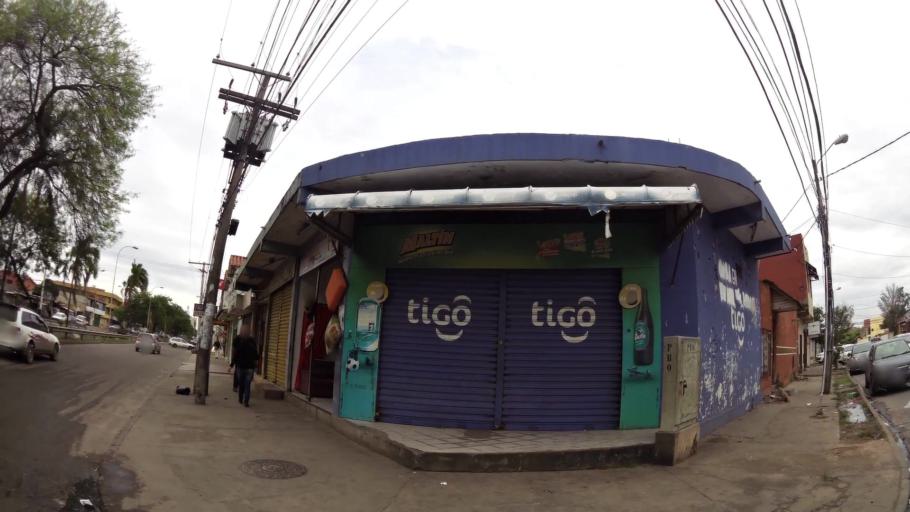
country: BO
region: Santa Cruz
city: Santa Cruz de la Sierra
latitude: -17.7664
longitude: -63.1626
